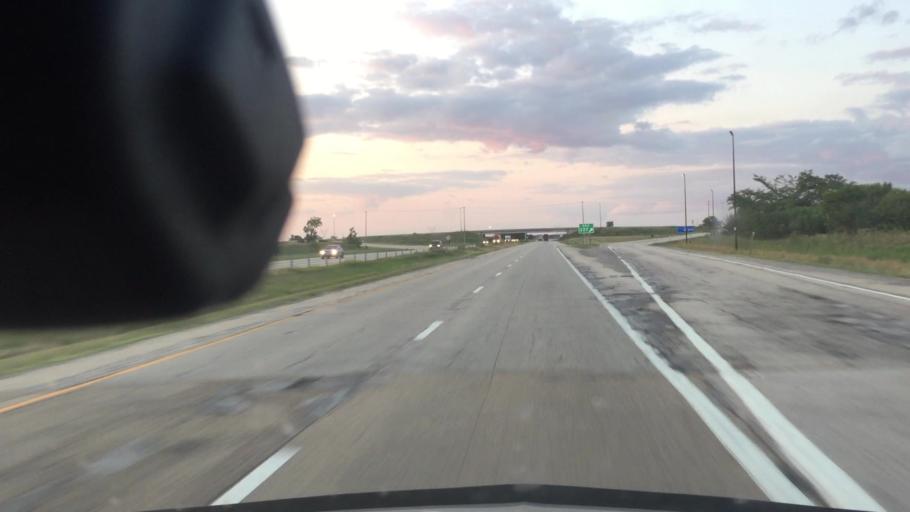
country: US
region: Illinois
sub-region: Grundy County
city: Gardner
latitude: 41.1808
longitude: -88.3228
